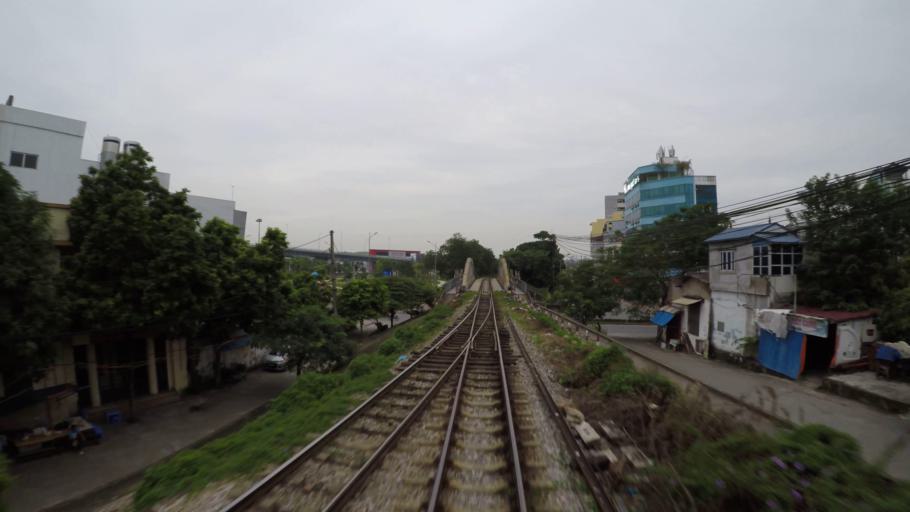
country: VN
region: Ha Noi
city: Trau Quy
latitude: 21.0195
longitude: 105.9404
